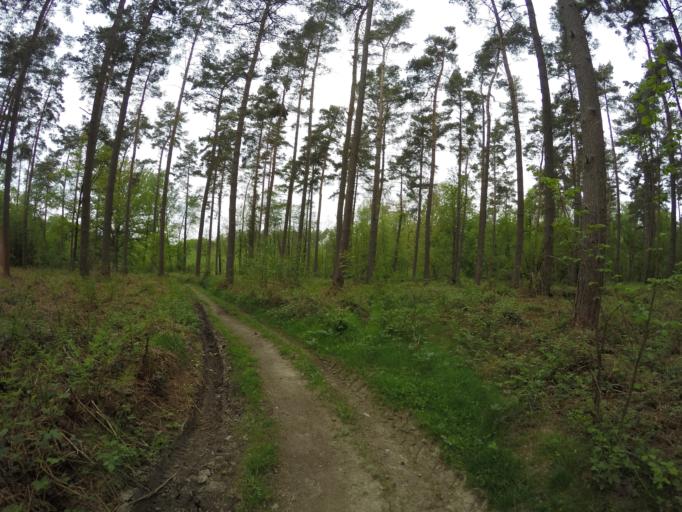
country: BE
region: Wallonia
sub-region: Province de Namur
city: Yvoir
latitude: 50.3355
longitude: 4.9473
